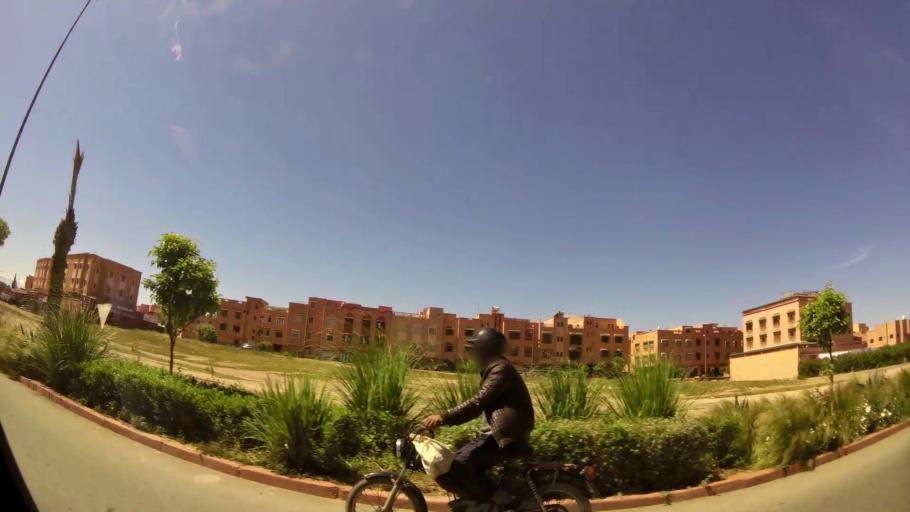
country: MA
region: Marrakech-Tensift-Al Haouz
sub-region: Marrakech
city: Marrakesh
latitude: 31.6612
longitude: -7.9854
